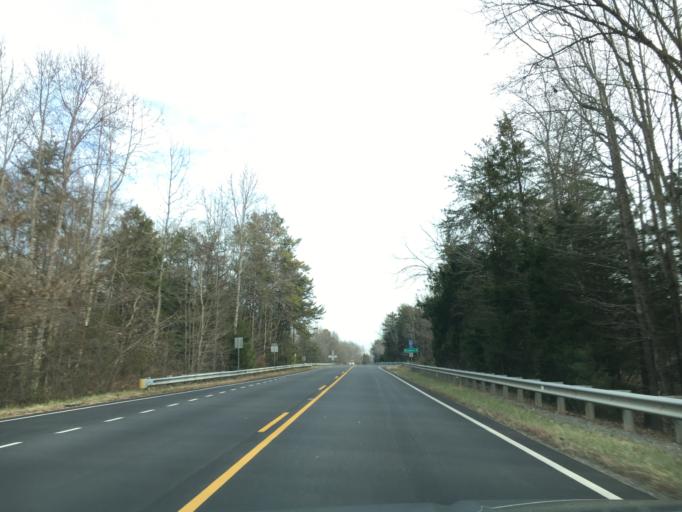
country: US
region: Virginia
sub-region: Goochland County
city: Goochland
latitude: 37.7797
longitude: -77.8907
